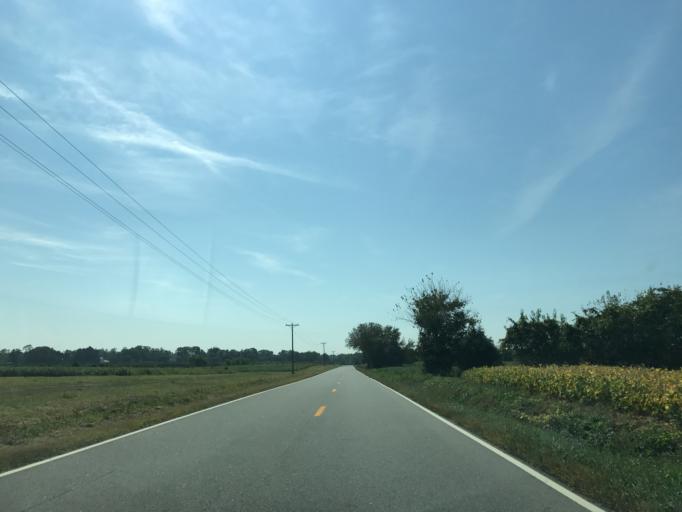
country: US
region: Maryland
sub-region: Queen Anne's County
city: Kingstown
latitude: 39.2981
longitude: -75.9299
